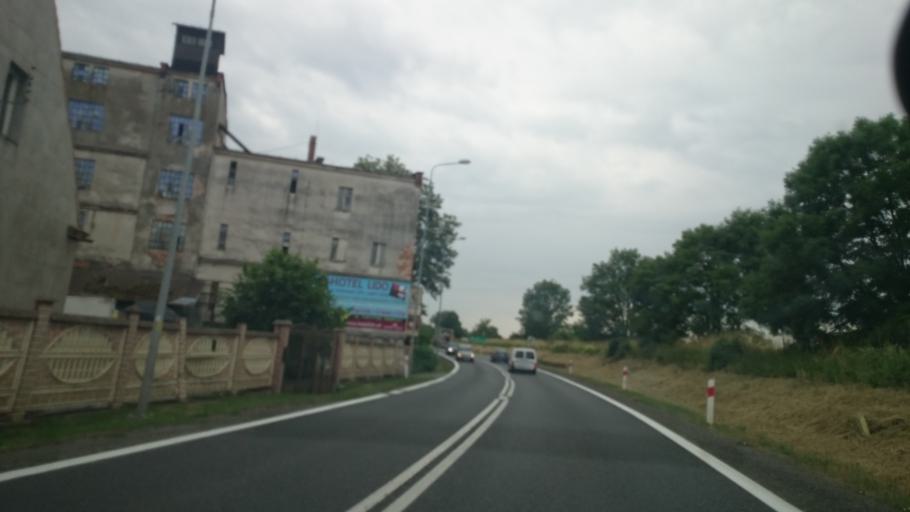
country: PL
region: Lower Silesian Voivodeship
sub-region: Powiat dzierzoniowski
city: Niemcza
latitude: 50.7434
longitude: 16.8403
